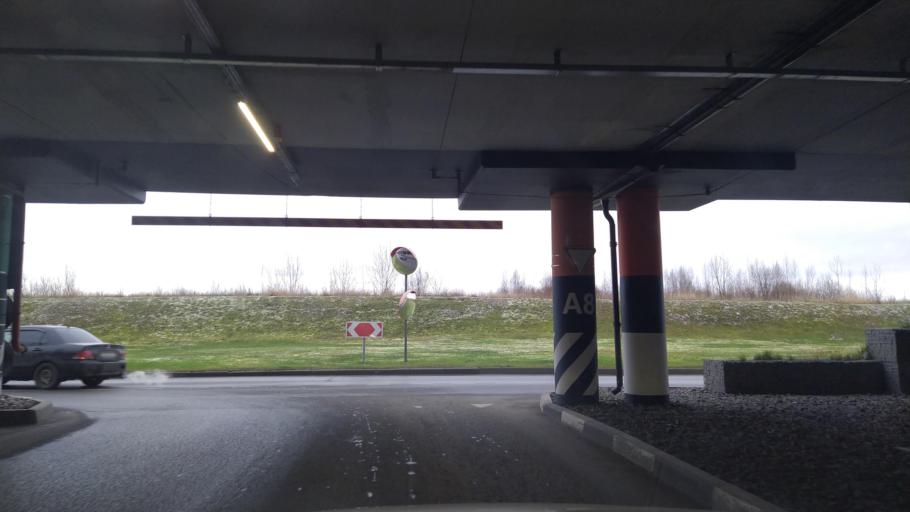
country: RU
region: Leningrad
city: Bugry
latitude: 60.0916
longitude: 30.3839
